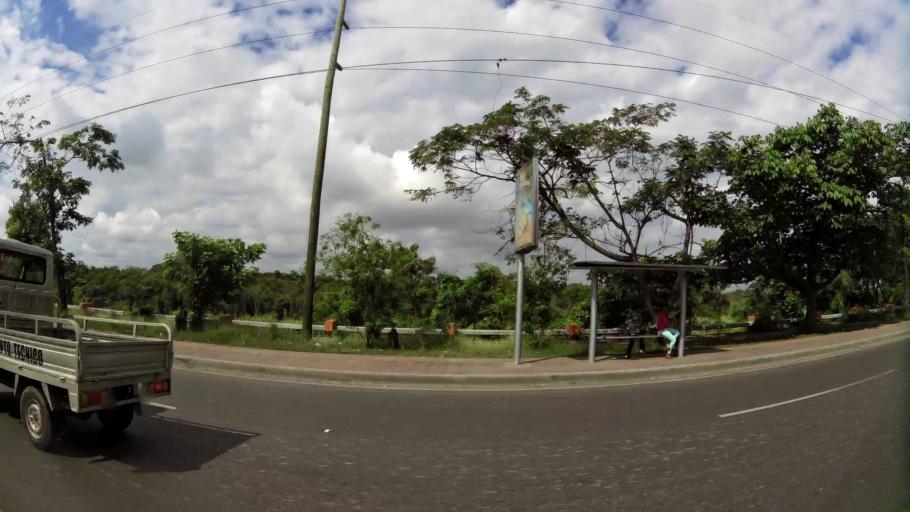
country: DO
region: Santiago
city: Santiago de los Caballeros
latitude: 19.4666
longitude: -70.7136
